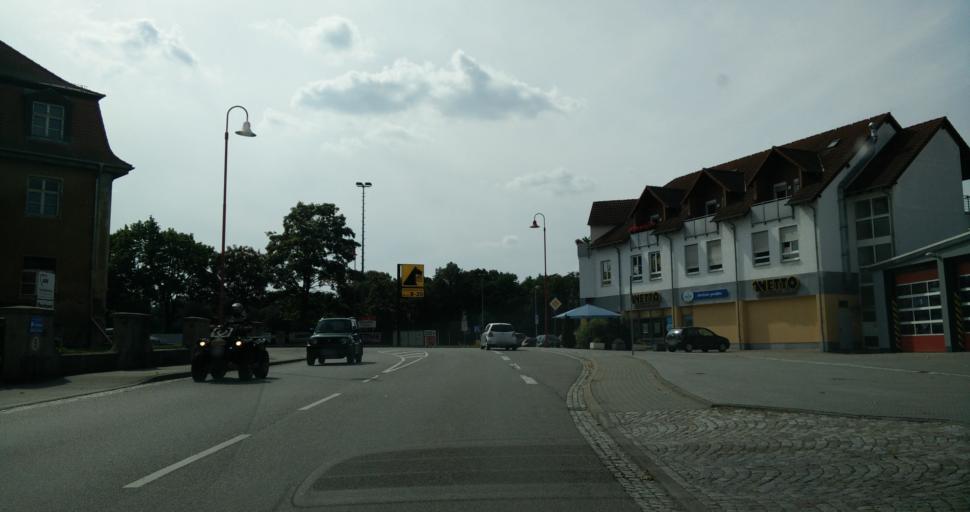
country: DE
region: Saxony
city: Colditz
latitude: 51.1284
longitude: 12.8027
